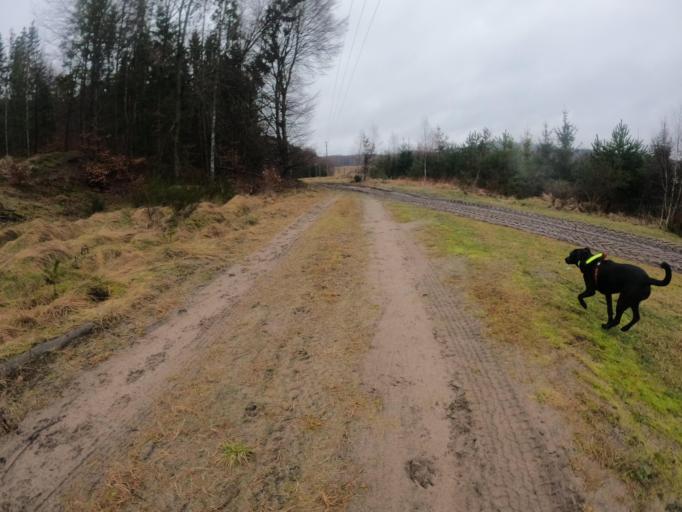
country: PL
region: West Pomeranian Voivodeship
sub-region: Powiat koszalinski
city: Polanow
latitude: 54.2280
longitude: 16.7246
